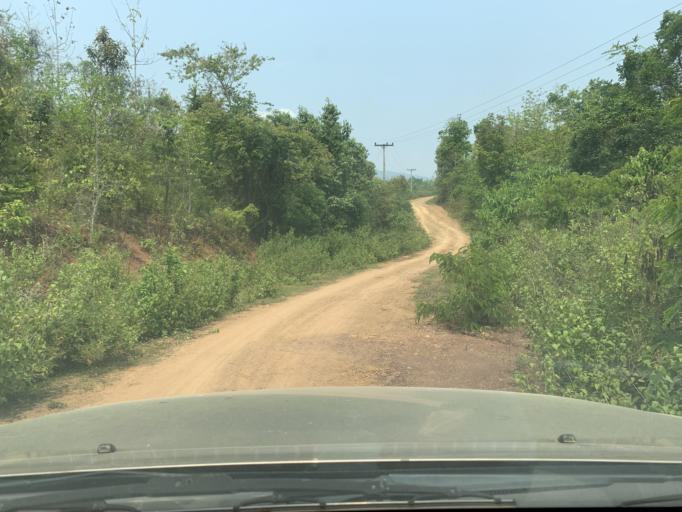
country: LA
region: Louangphabang
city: Louangphabang
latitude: 19.9526
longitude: 102.1283
